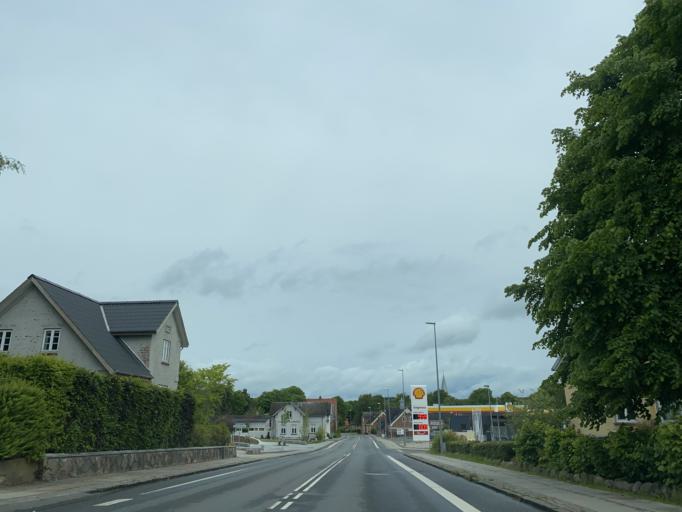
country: DK
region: Central Jutland
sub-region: Favrskov Kommune
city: Hammel
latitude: 56.2529
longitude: 9.8610
